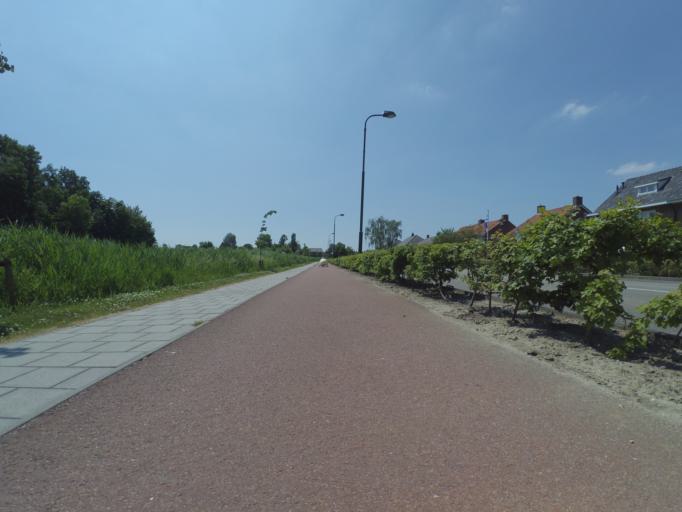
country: NL
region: Zeeland
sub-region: Gemeente Tholen
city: Tholen
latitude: 51.5332
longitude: 4.2165
